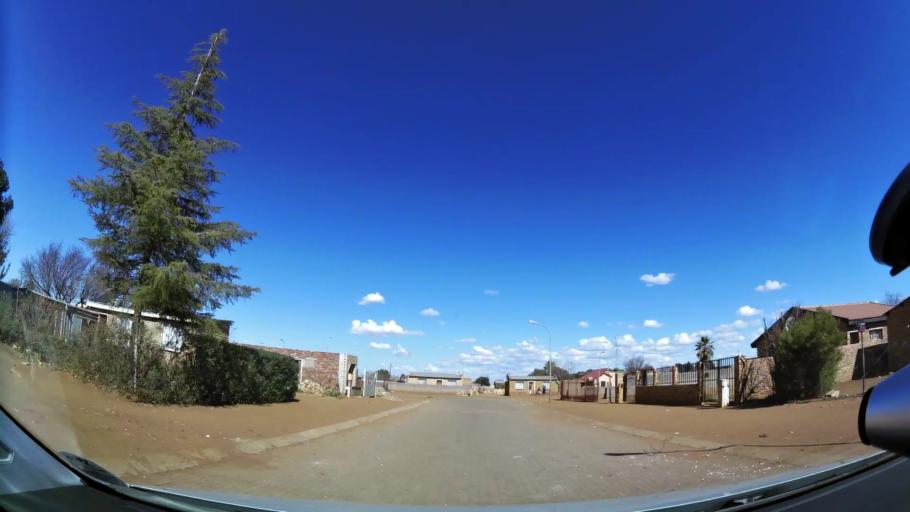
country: ZA
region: North-West
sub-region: Dr Kenneth Kaunda District Municipality
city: Klerksdorp
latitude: -26.8683
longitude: 26.5808
